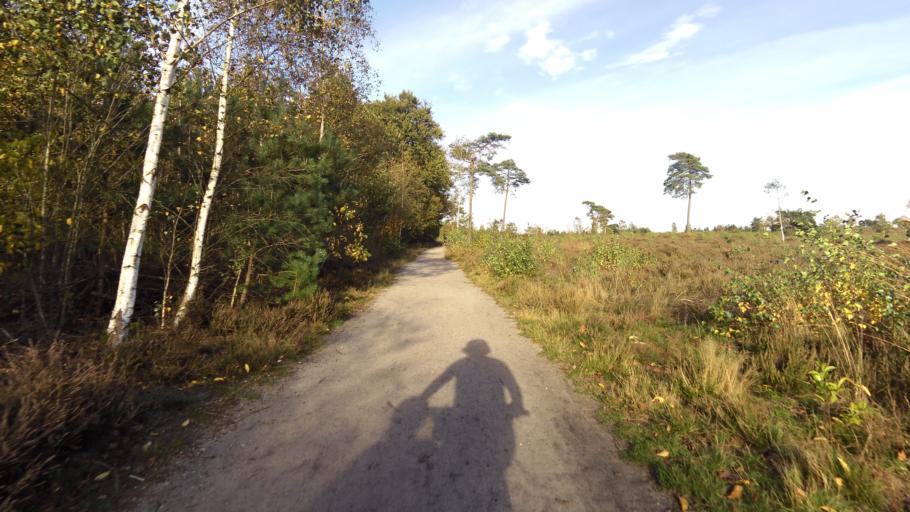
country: NL
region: Gelderland
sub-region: Gemeente Heerde
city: Heerde
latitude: 52.4114
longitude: 6.0297
